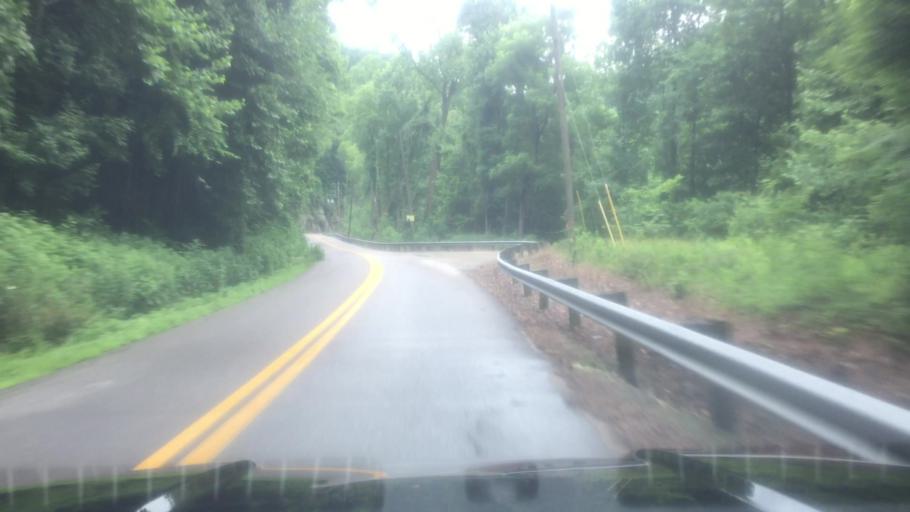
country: US
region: West Virginia
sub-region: Kanawha County
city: Montgomery
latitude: 38.1052
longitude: -81.3844
